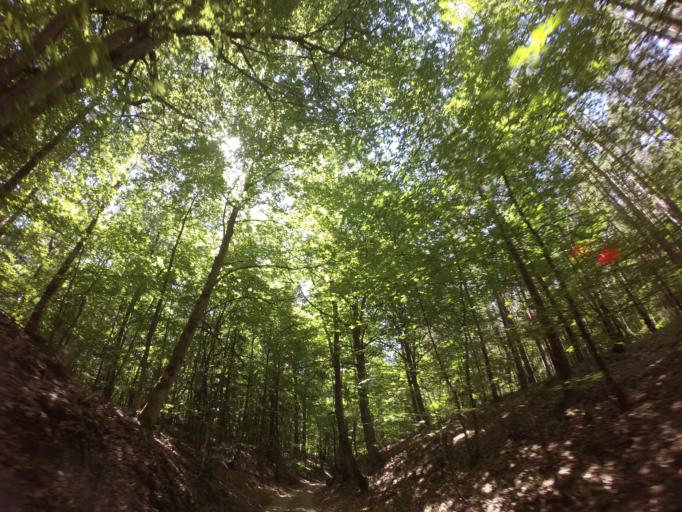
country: PL
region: West Pomeranian Voivodeship
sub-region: Powiat choszczenski
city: Drawno
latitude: 53.1631
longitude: 15.8748
